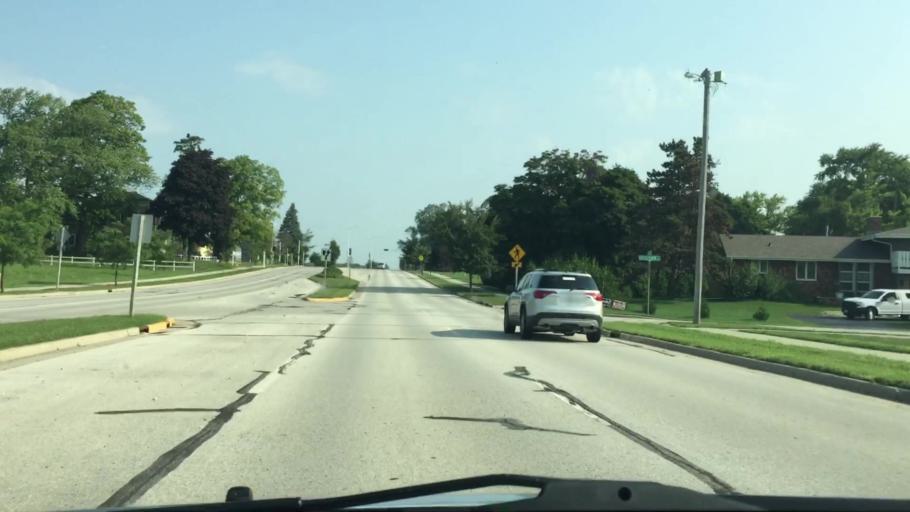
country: US
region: Wisconsin
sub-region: Waukesha County
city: Brookfield
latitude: 43.0294
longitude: -88.1269
